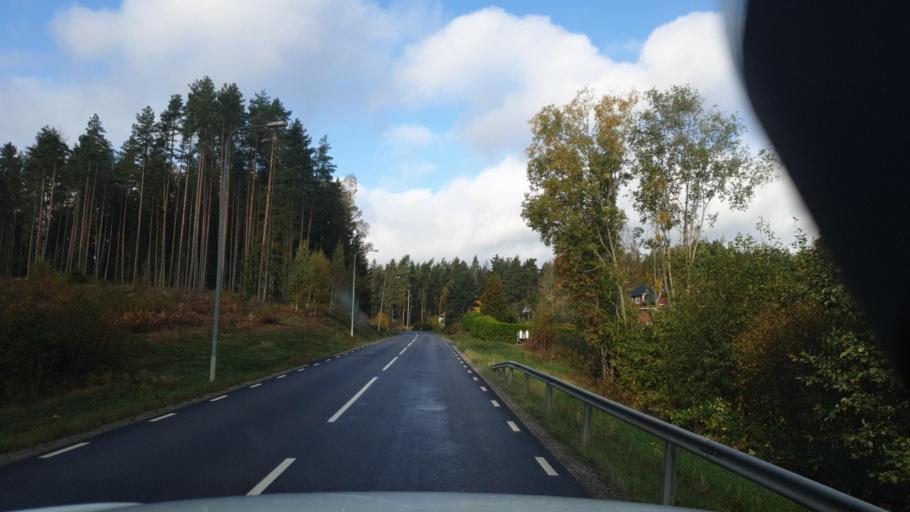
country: SE
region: Vaermland
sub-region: Arvika Kommun
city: Arvika
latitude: 59.5376
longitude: 12.5923
